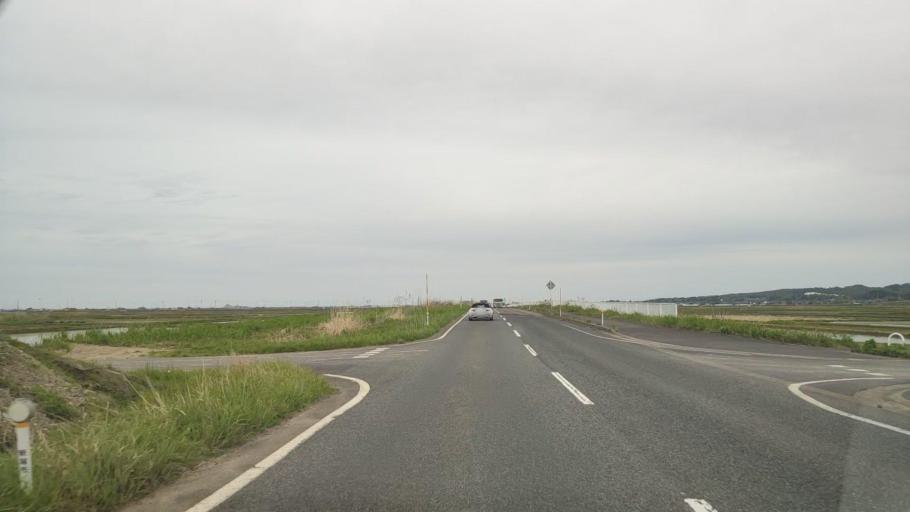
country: JP
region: Niigata
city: Niitsu-honcho
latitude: 37.7607
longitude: 139.0949
